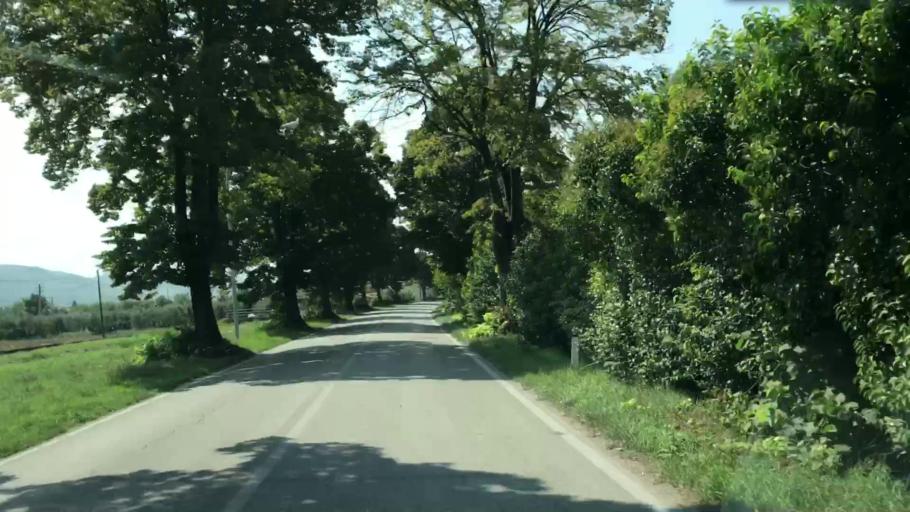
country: IT
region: The Marches
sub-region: Provincia di Ascoli Piceno
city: Pagliare
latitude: 42.8763
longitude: 13.7766
